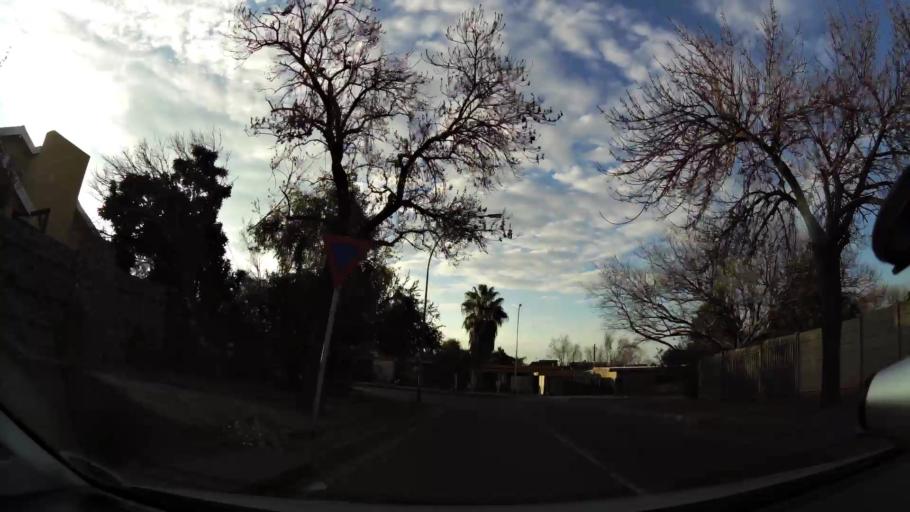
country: ZA
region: Orange Free State
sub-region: Mangaung Metropolitan Municipality
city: Bloemfontein
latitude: -29.1412
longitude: 26.1849
